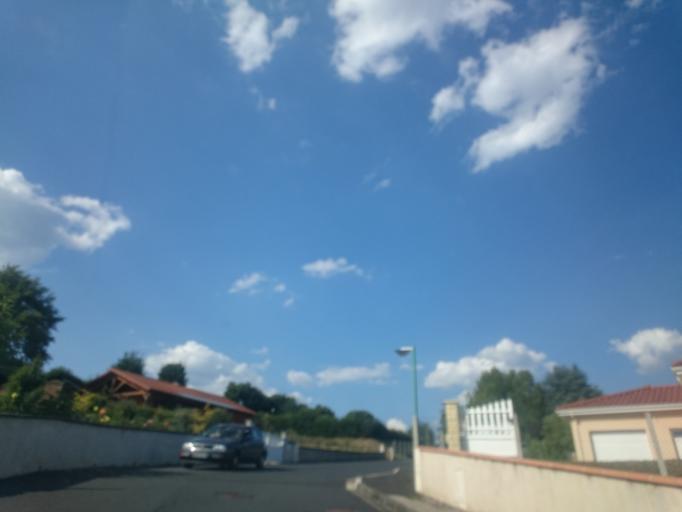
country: FR
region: Auvergne
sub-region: Departement du Cantal
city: Saint-Mamet-la-Salvetat
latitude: 44.8577
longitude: 2.2258
